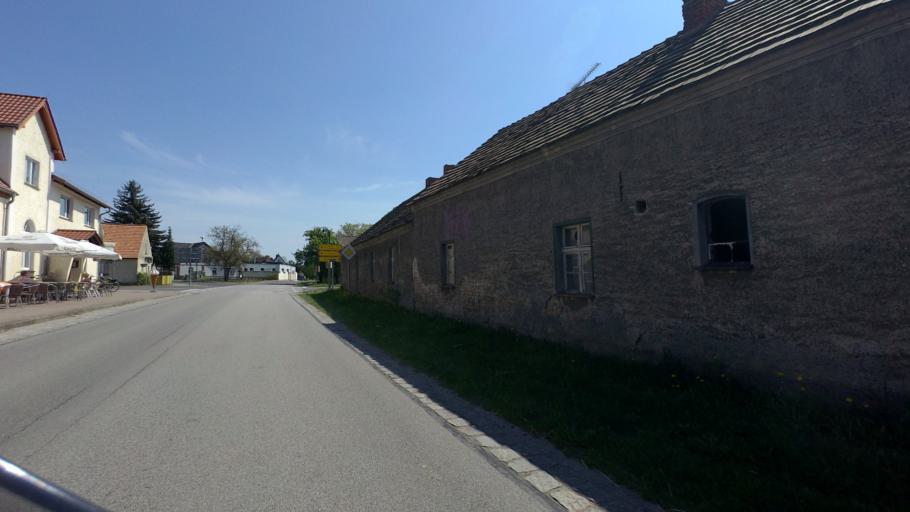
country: DE
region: Brandenburg
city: Schlepzig
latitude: 52.0591
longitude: 13.9575
